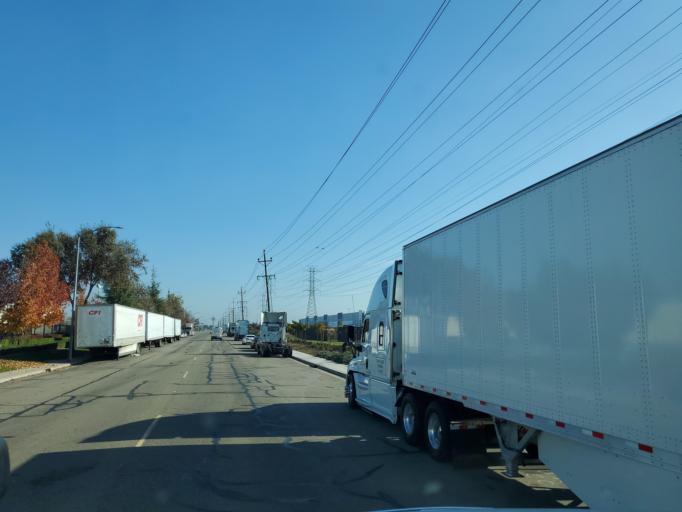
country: US
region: California
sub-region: San Joaquin County
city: Kennedy
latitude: 37.9161
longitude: -121.2521
